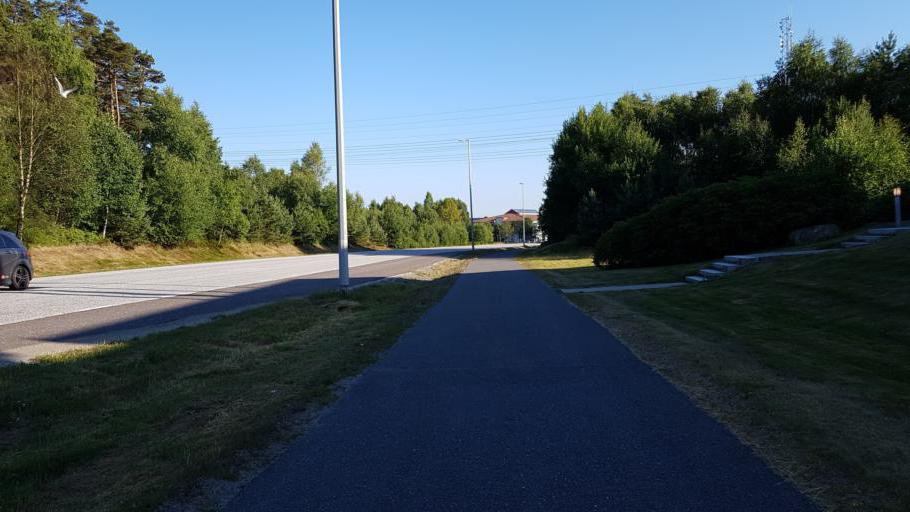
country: SE
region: Vaestra Goetaland
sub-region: Harryda Kommun
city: Molnlycke
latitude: 57.6778
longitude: 12.0944
